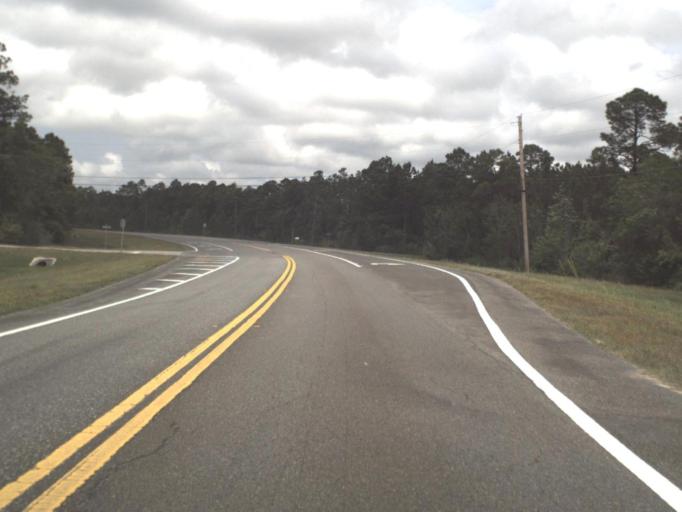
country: US
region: Florida
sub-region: Santa Rosa County
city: Bagdad
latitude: 30.5077
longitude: -87.0816
